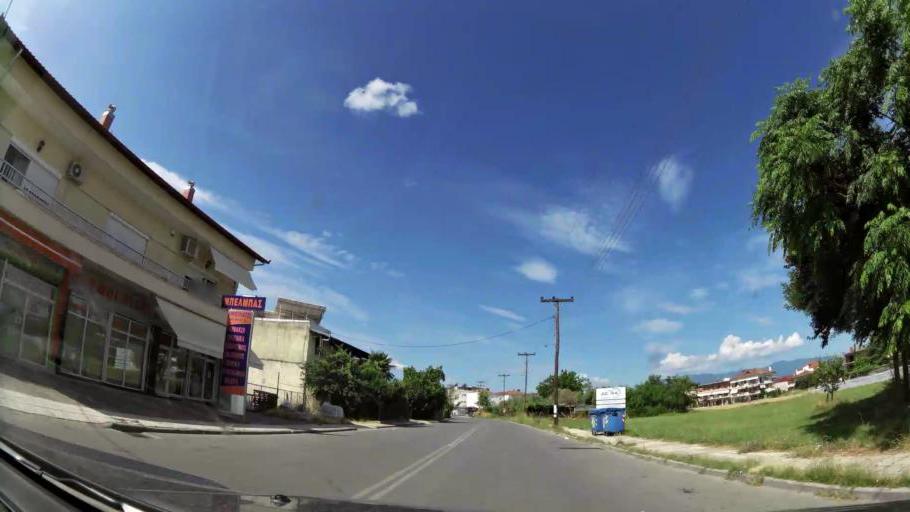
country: GR
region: Central Macedonia
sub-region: Nomos Pierias
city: Katerini
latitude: 40.2780
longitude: 22.4939
